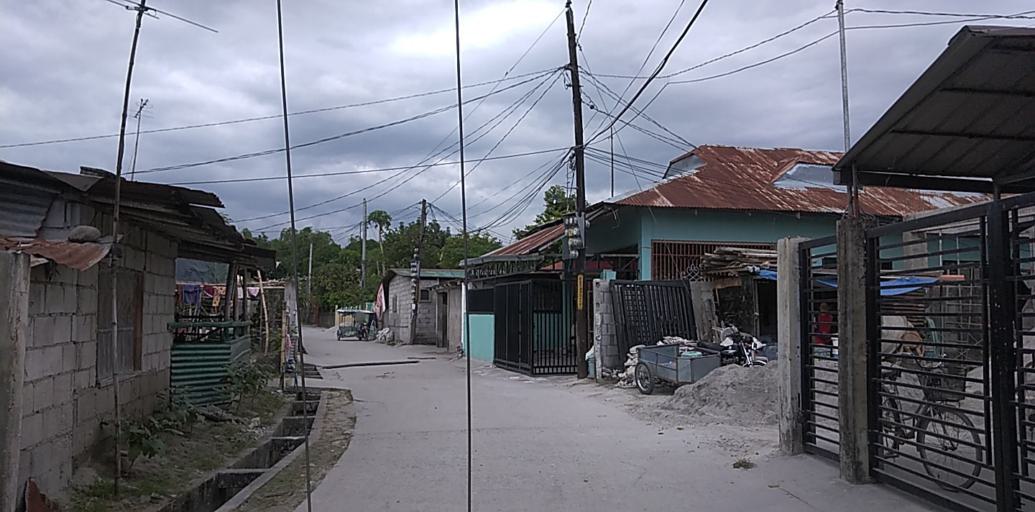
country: PH
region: Central Luzon
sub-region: Province of Pampanga
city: Pulung Santol
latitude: 15.0404
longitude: 120.5663
